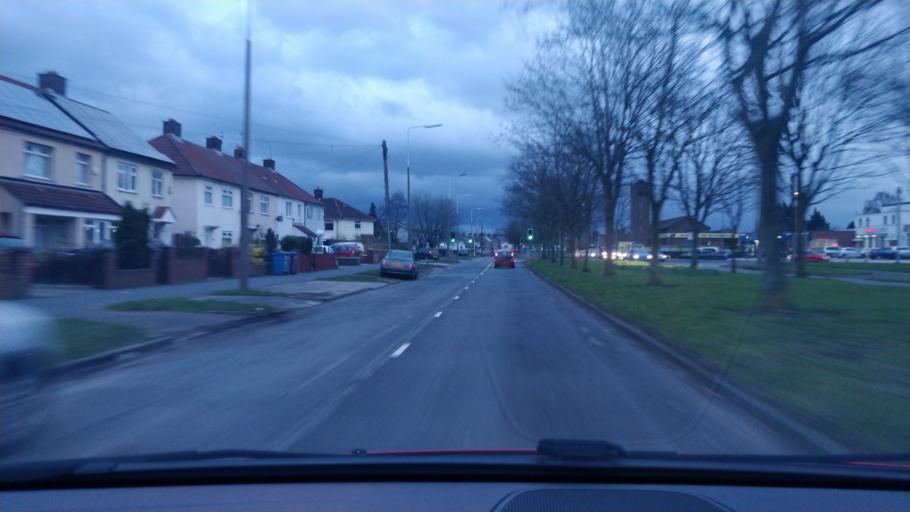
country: GB
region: England
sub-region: Knowsley
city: Knowsley
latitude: 53.4319
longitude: -2.8794
